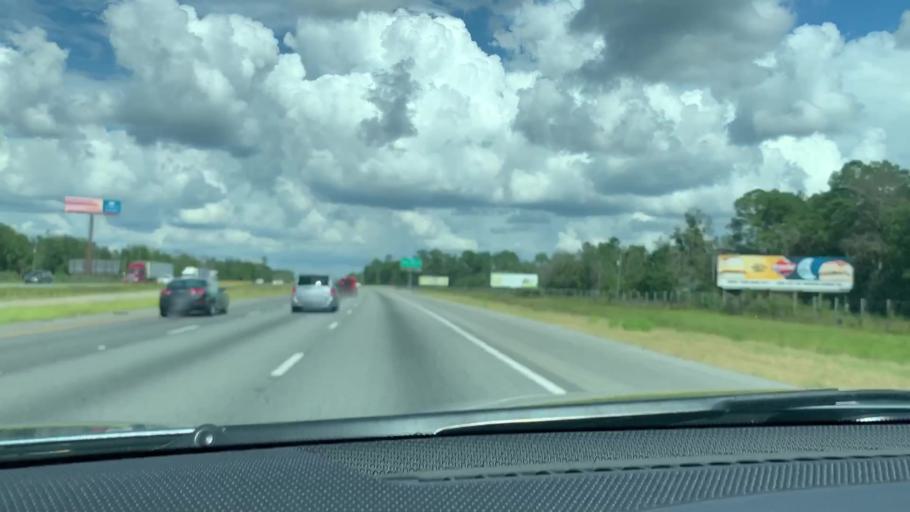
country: US
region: Georgia
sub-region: Glynn County
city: Brunswick
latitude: 31.0905
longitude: -81.6052
